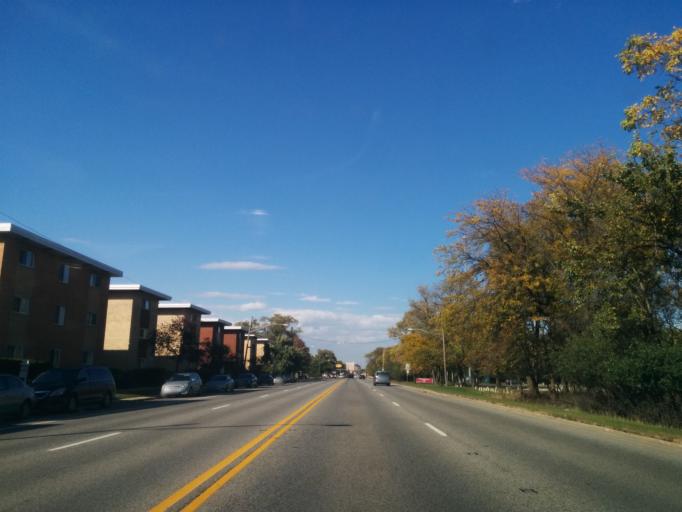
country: US
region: Illinois
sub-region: Cook County
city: Schiller Park
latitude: 41.9614
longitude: -87.8612
